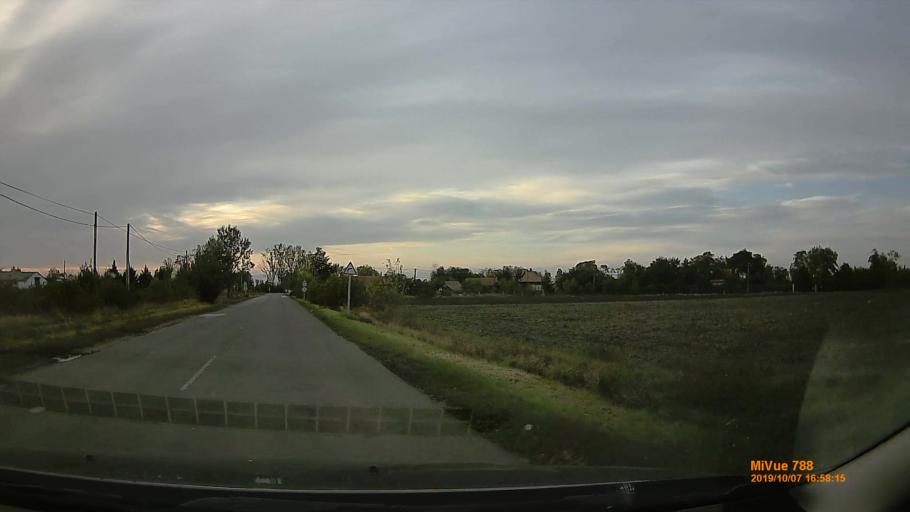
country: HU
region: Bekes
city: Szarvas
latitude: 46.8299
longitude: 20.5824
